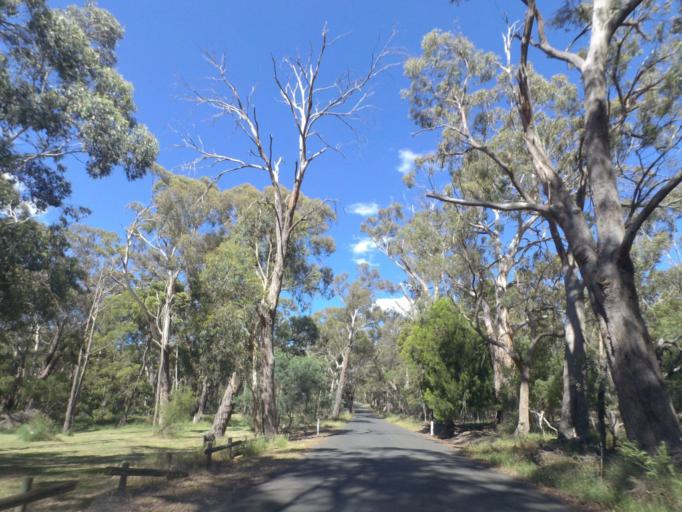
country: AU
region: Victoria
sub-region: Hume
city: Sunbury
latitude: -37.4213
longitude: 144.6203
